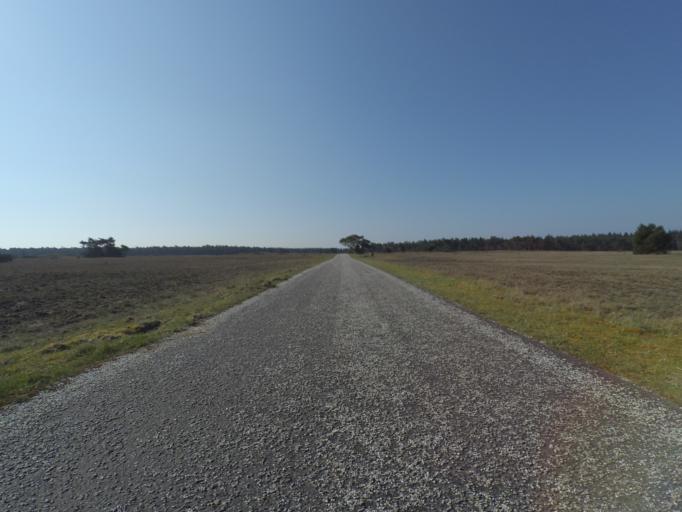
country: NL
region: Gelderland
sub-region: Gemeente Ede
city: Otterlo
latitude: 52.1076
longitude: 5.8035
